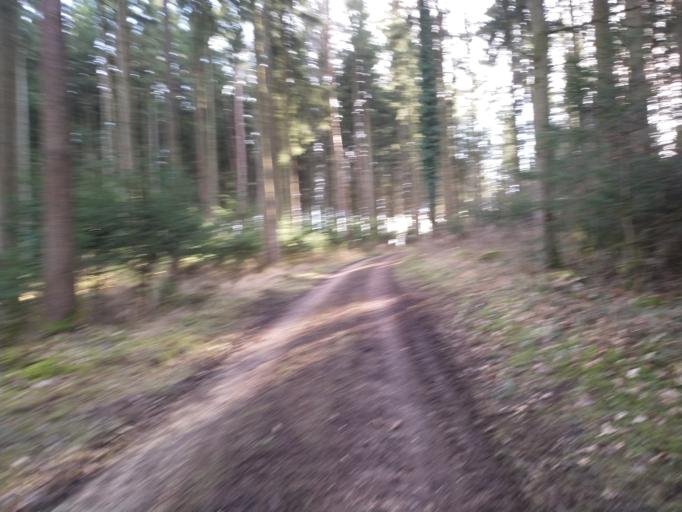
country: DE
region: Bavaria
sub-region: Swabia
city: Rettenbach
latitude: 48.4307
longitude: 10.3210
